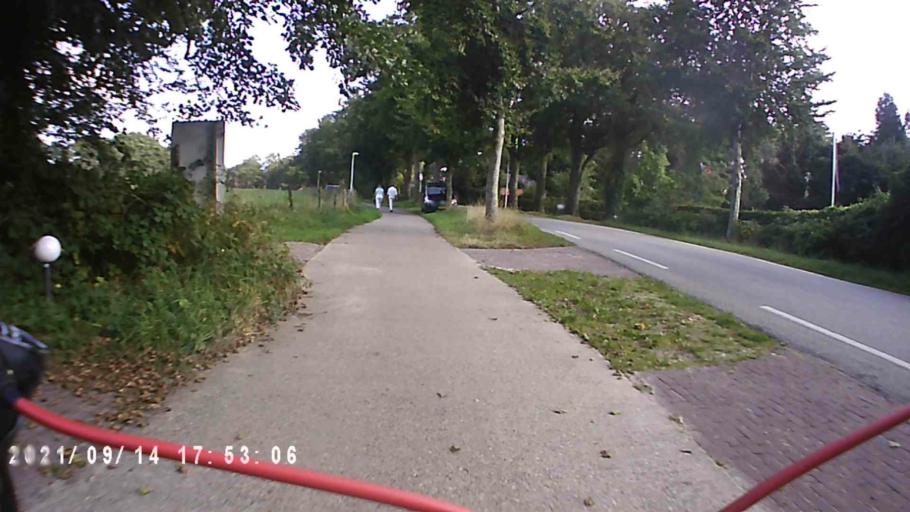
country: NL
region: Groningen
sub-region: Gemeente Haren
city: Haren
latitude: 53.1316
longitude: 6.6329
